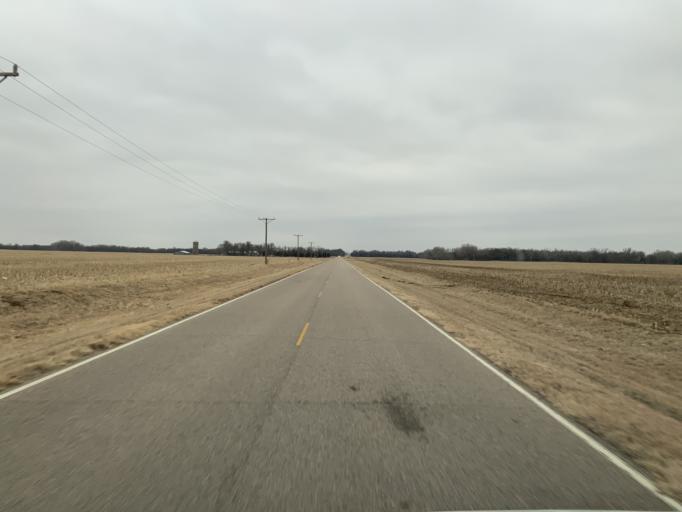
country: US
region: Kansas
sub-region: Reno County
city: South Hutchinson
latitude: 37.9481
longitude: -98.0873
